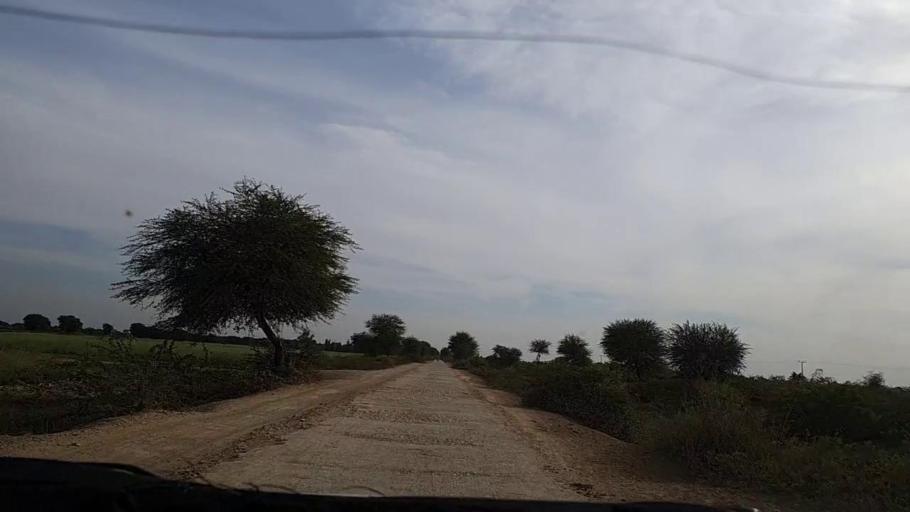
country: PK
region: Sindh
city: Dhoro Naro
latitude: 25.4248
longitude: 69.5216
